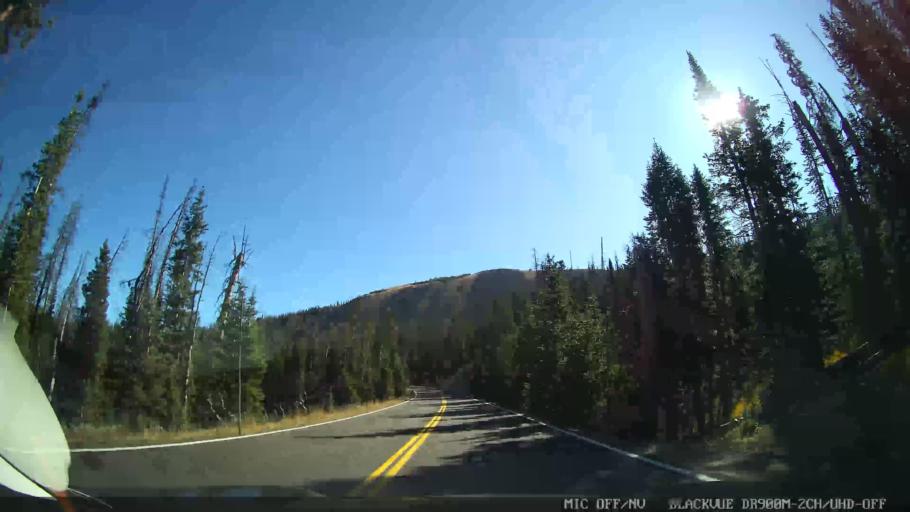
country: US
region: Colorado
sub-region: Larimer County
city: Estes Park
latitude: 40.4282
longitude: -105.8016
